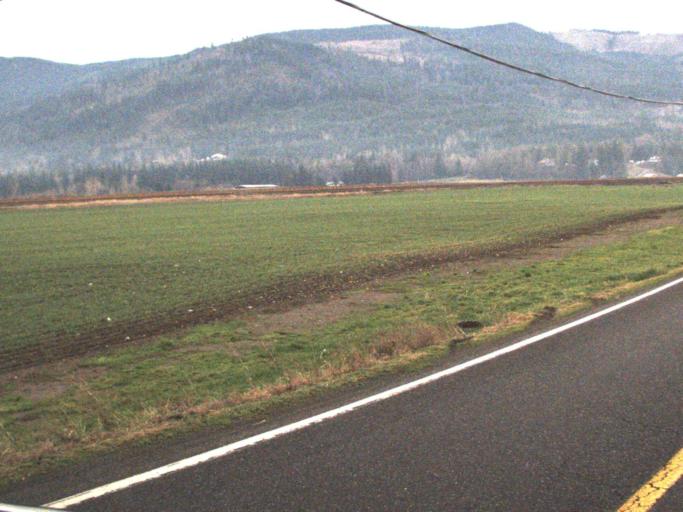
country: US
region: Washington
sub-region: Whatcom County
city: Nooksack
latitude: 48.8654
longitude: -122.3086
